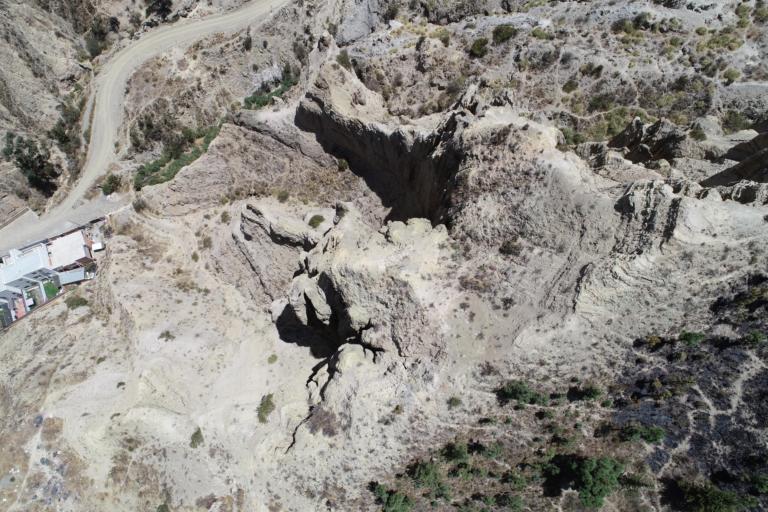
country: BO
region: La Paz
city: La Paz
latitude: -16.5224
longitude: -68.0770
